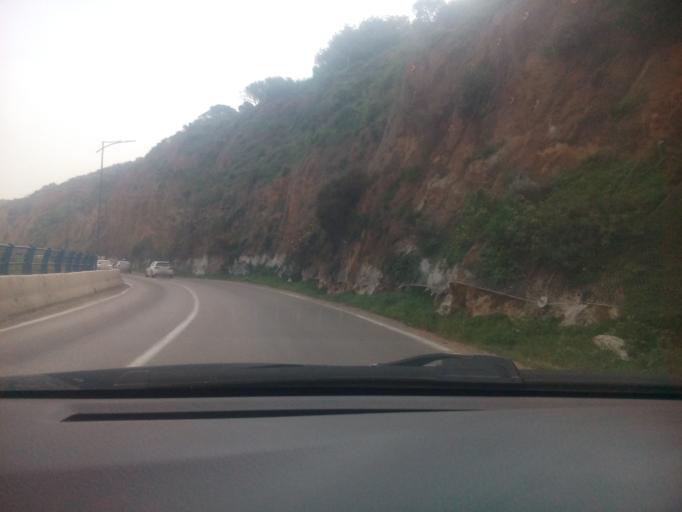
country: DZ
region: Oran
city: Oran
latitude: 35.7135
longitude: -0.6621
